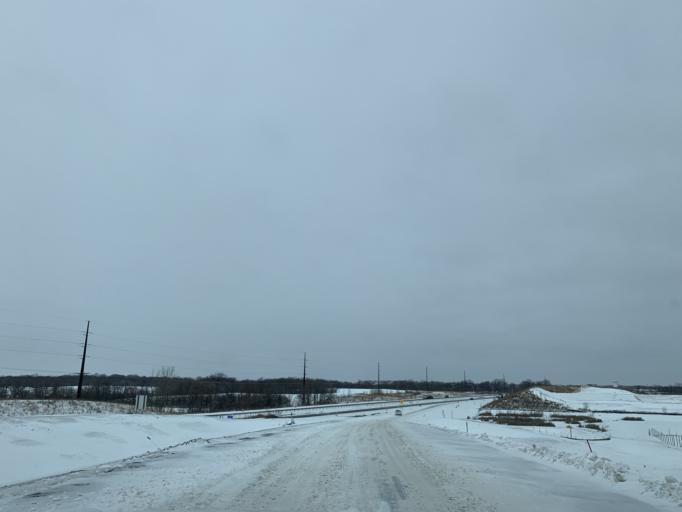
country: US
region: Minnesota
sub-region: Carver County
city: Carver
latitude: 44.7914
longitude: -93.6306
